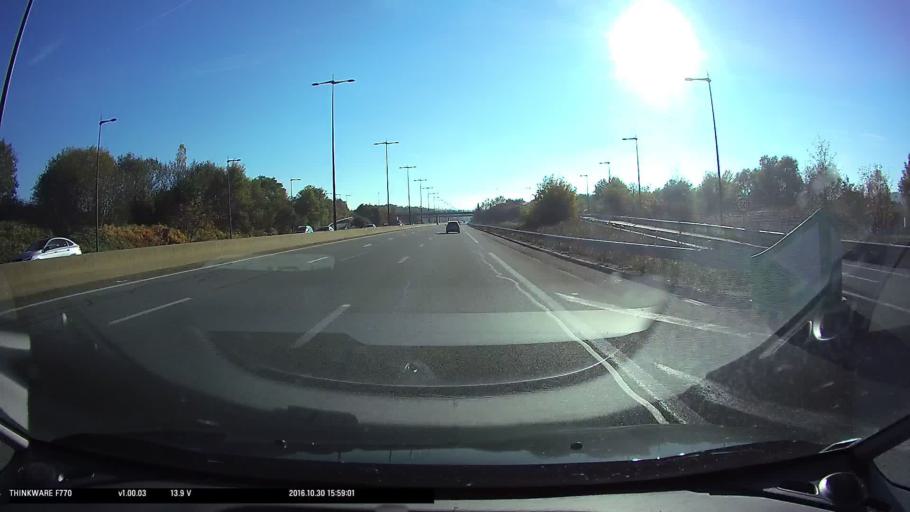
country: FR
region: Franche-Comte
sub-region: Departement du Doubs
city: Nommay
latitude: 47.5280
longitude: 6.8578
